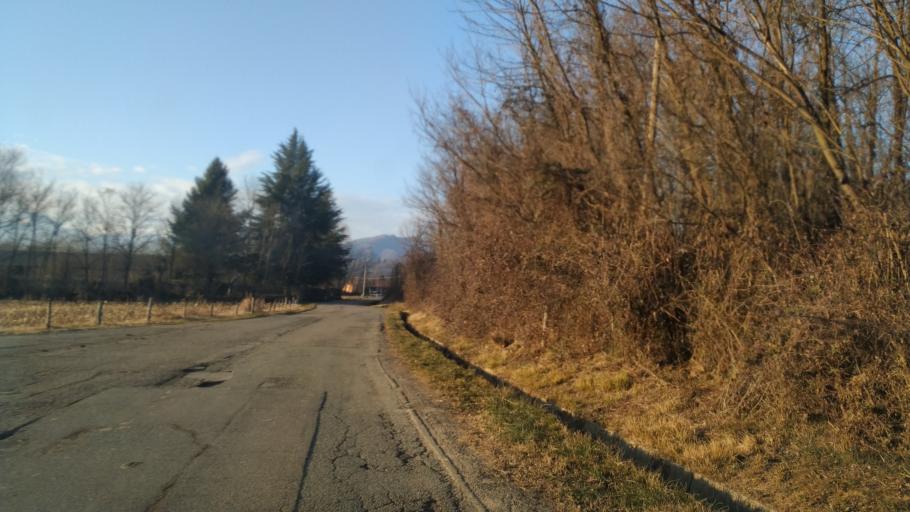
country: IT
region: Piedmont
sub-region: Provincia di Novara
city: Prato Sesia
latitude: 45.6630
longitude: 8.3732
